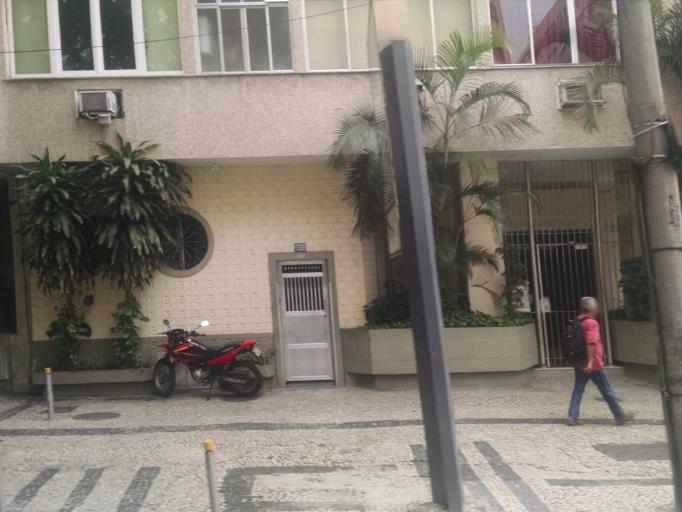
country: BR
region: Rio de Janeiro
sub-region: Rio De Janeiro
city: Rio de Janeiro
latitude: -22.9848
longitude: -43.1905
